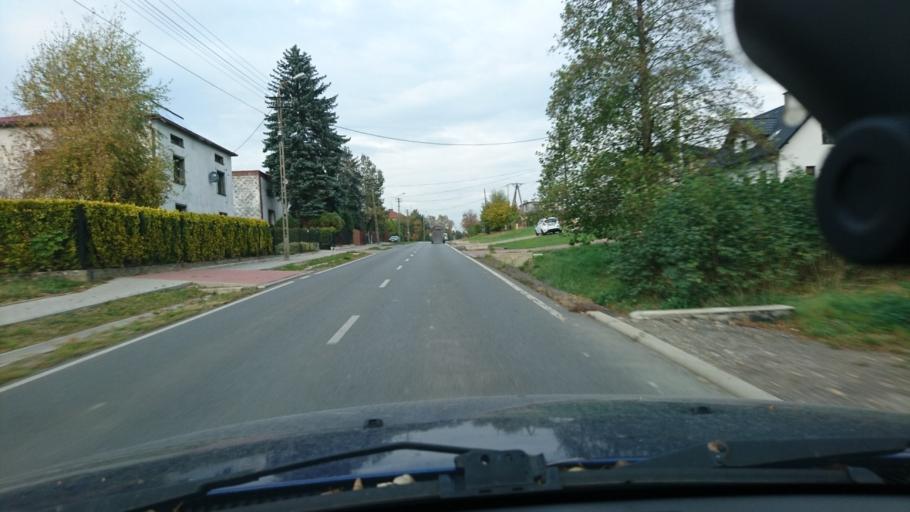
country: PL
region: Silesian Voivodeship
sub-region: Powiat bielski
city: Kozy
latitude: 49.8610
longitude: 19.1556
